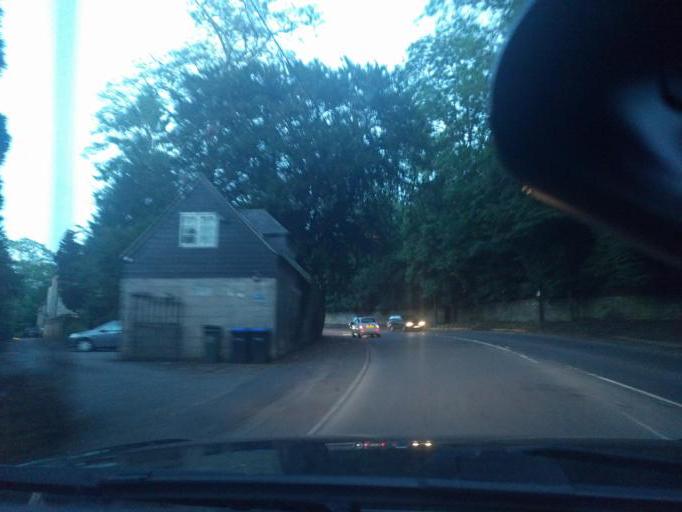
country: GB
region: England
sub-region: Wiltshire
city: Box
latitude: 51.4144
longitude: -2.2571
